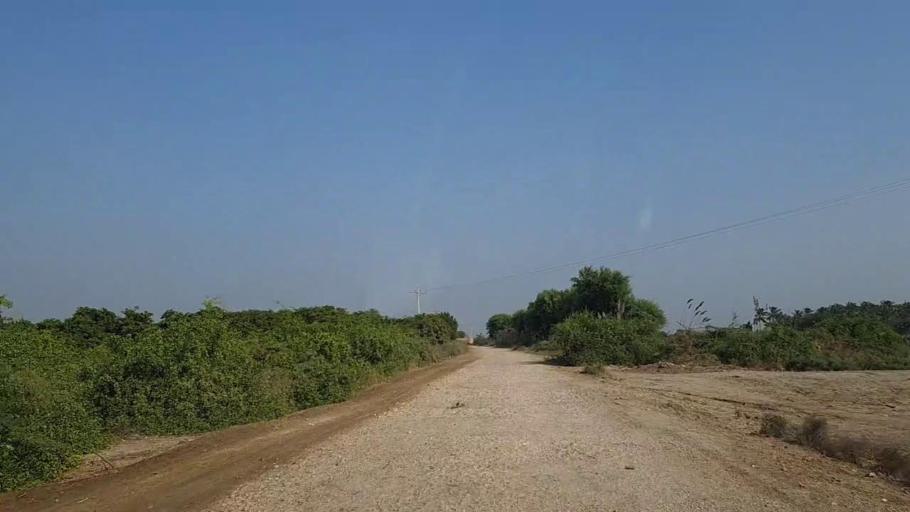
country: PK
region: Sindh
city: Mirpur Sakro
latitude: 24.6195
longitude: 67.6643
